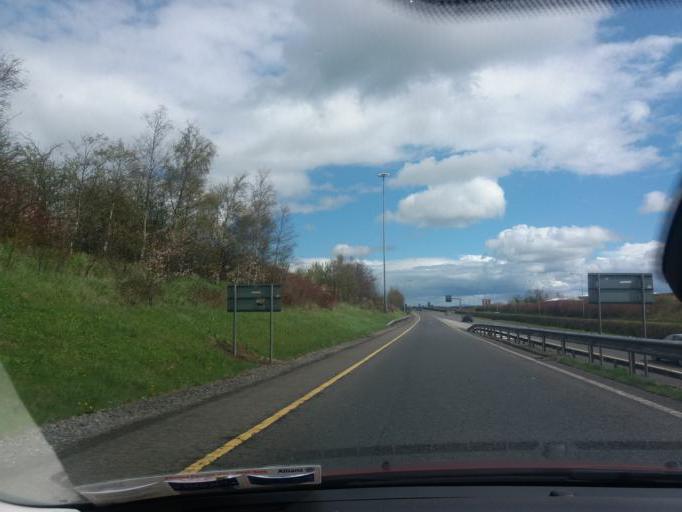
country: IE
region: Leinster
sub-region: Kildare
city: Cherryville
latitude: 53.1468
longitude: -7.0110
